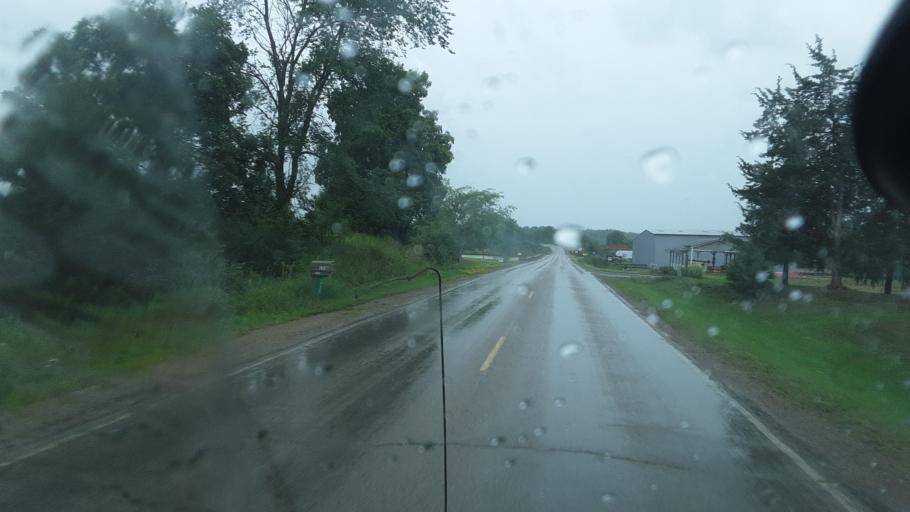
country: US
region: Ohio
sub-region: Williams County
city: Pioneer
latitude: 41.7089
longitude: -84.6449
